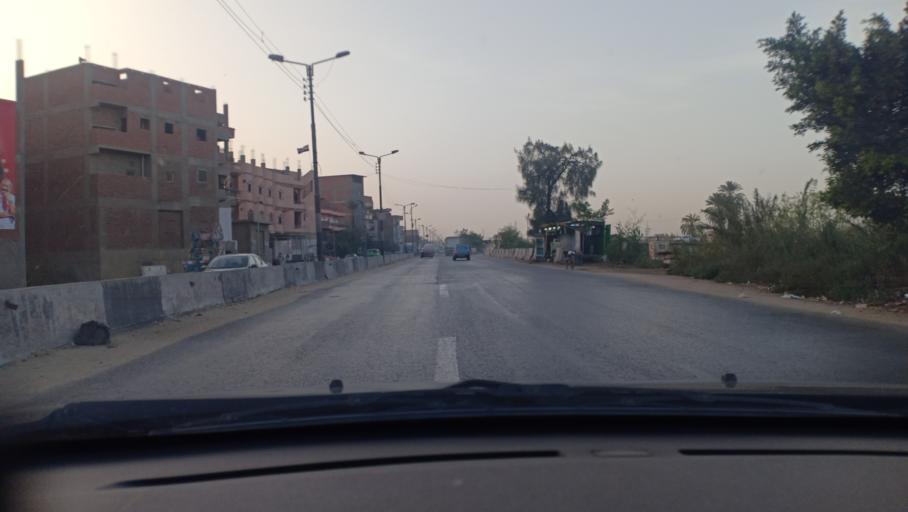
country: EG
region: Muhafazat al Gharbiyah
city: Zifta
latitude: 30.6815
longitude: 31.2819
